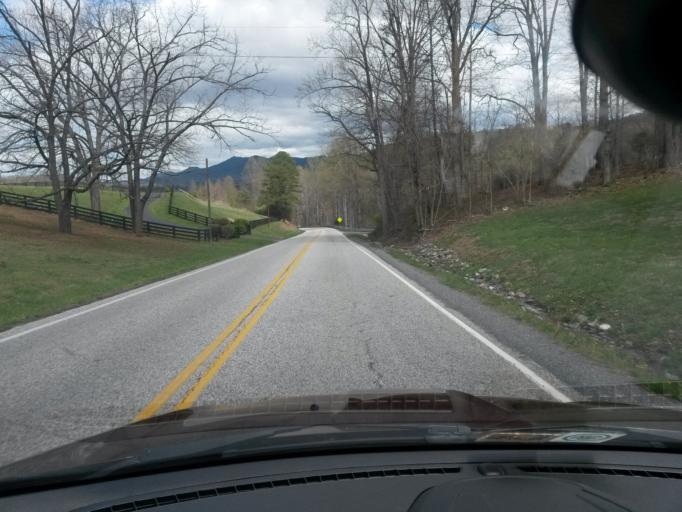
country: US
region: Virginia
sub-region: City of Buena Vista
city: Buena Vista
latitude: 37.6994
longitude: -79.3887
